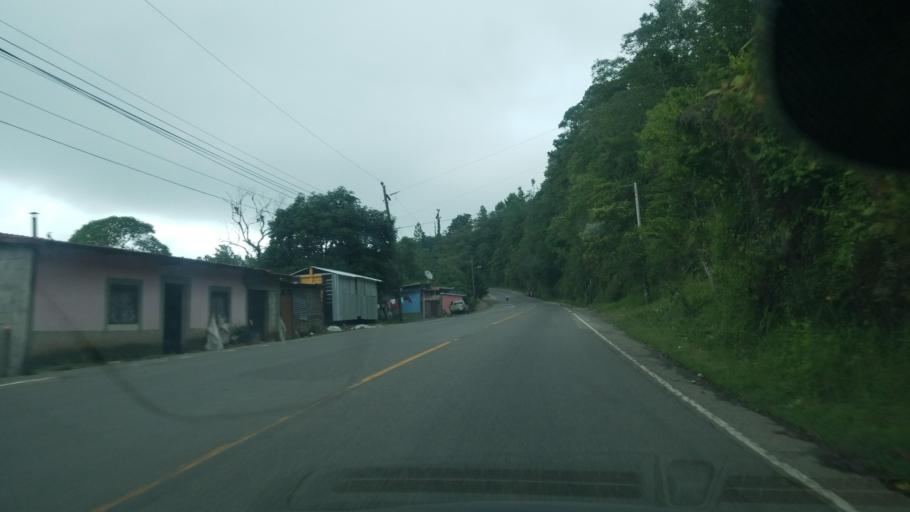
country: HN
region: Ocotepeque
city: La Labor
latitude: 14.4815
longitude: -89.0557
